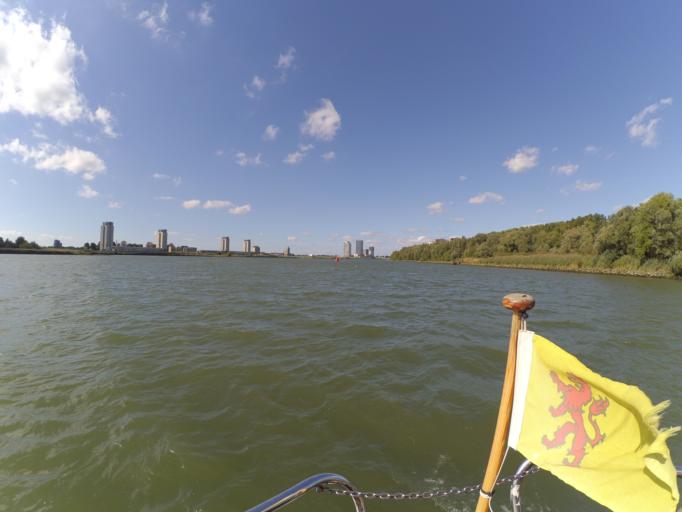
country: NL
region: South Holland
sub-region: Gemeente Spijkenisse
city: Spijkenisse
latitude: 51.8461
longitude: 4.3658
